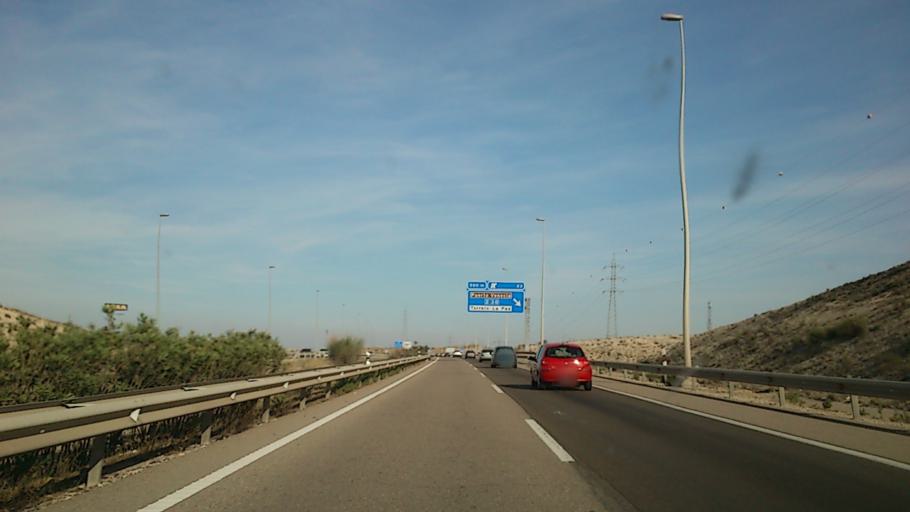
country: ES
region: Aragon
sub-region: Provincia de Zaragoza
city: Cuarte de Huerva
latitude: 41.6055
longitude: -0.9002
